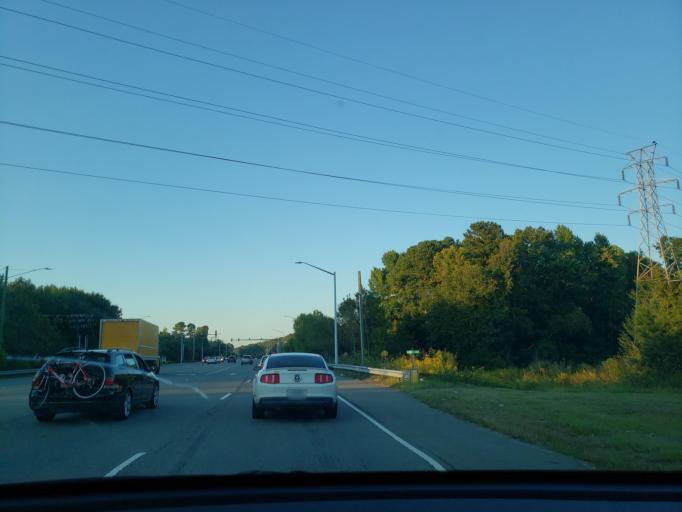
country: US
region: North Carolina
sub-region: Durham County
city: Durham
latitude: 35.9093
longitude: -78.8932
